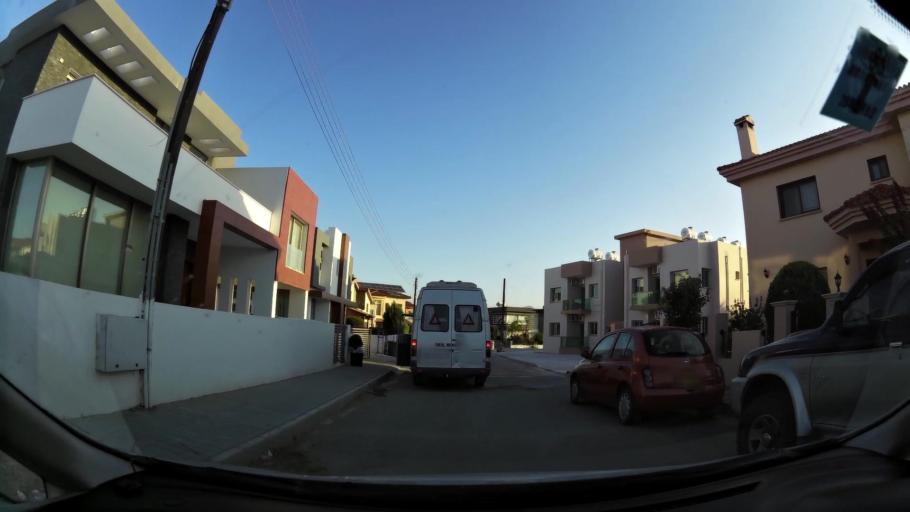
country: CY
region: Lefkosia
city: Nicosia
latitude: 35.1926
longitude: 33.3176
